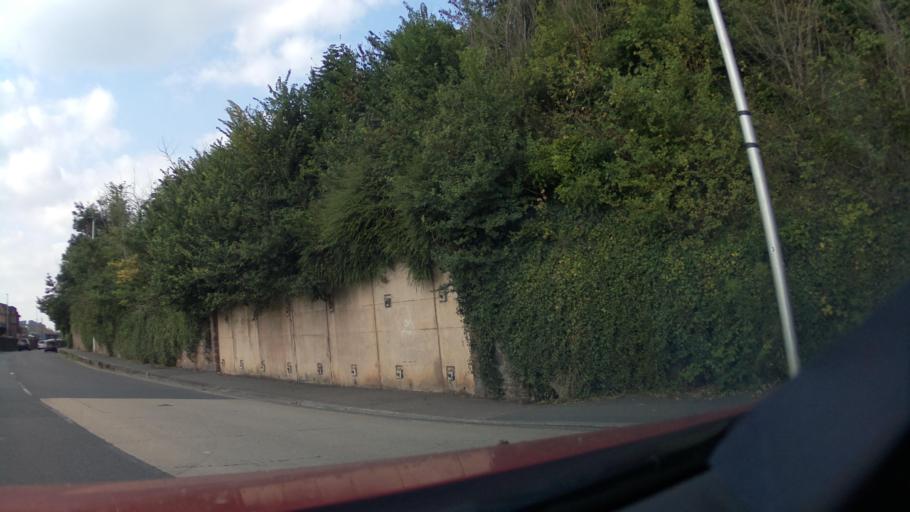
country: GB
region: England
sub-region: Devon
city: Exeter
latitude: 50.7310
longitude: -3.5426
